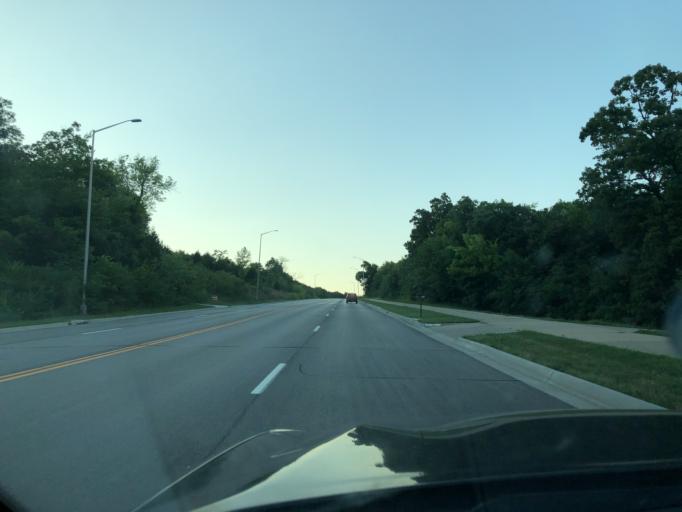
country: US
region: Kansas
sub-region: Leavenworth County
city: Leavenworth
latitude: 39.2958
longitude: -94.9511
